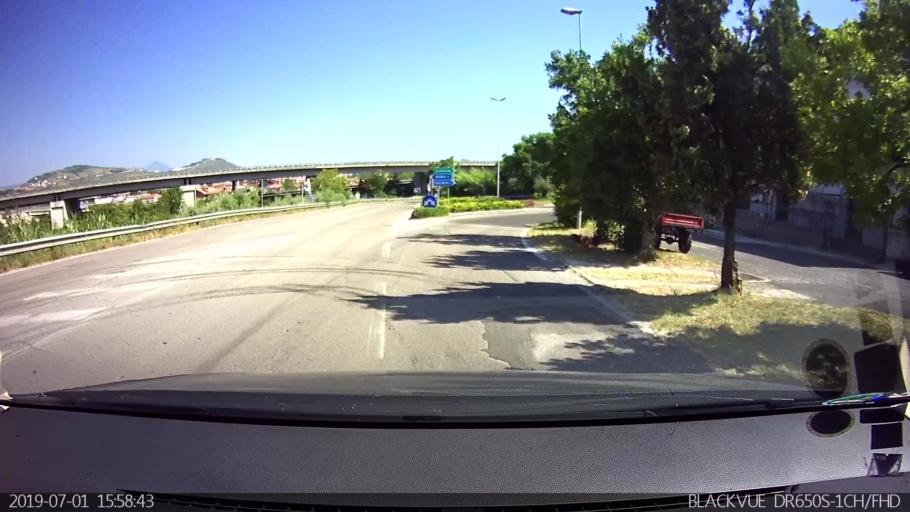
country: IT
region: Latium
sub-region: Provincia di Frosinone
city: Sant'Angelo in Villa-Giglio
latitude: 41.6657
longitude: 13.4242
